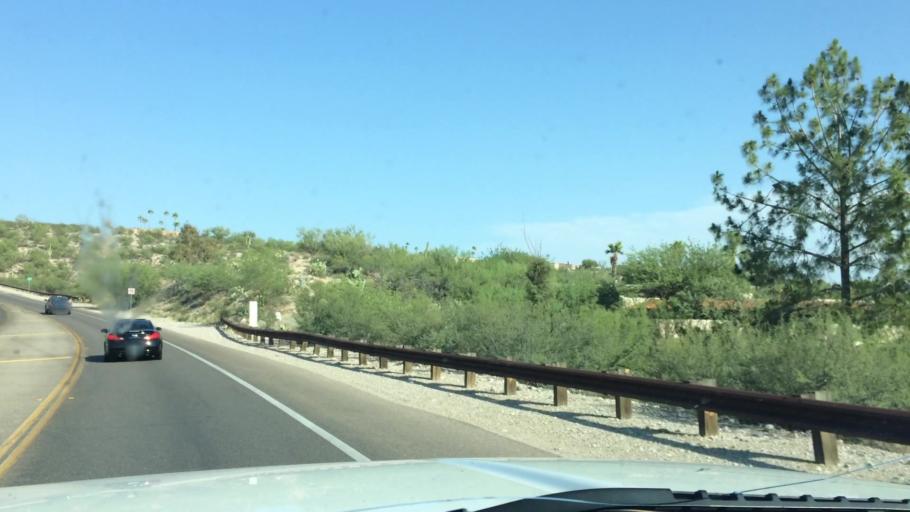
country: US
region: Arizona
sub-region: Pima County
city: Catalina Foothills
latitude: 32.3063
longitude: -110.8690
